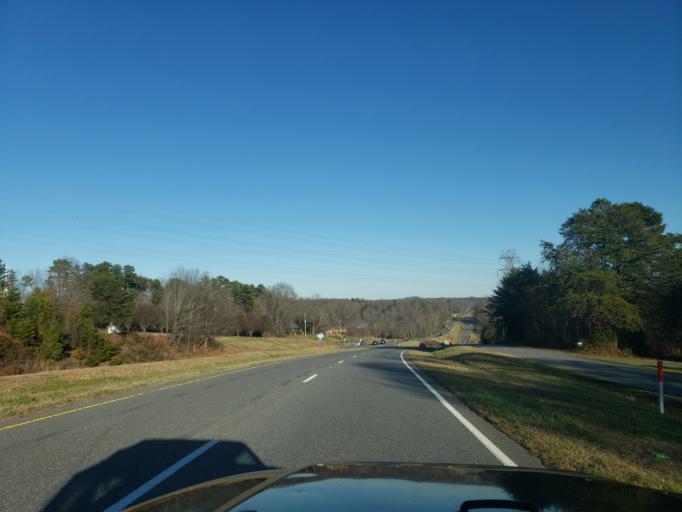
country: US
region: North Carolina
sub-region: Gaston County
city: Bessemer City
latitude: 35.2534
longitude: -81.2768
